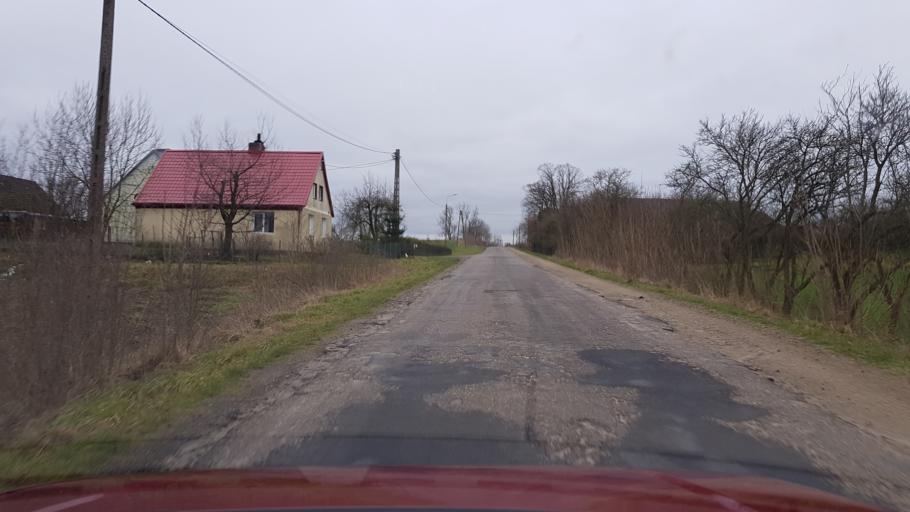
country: PL
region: West Pomeranian Voivodeship
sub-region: Powiat koszalinski
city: Mielno
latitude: 54.1836
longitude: 16.0175
